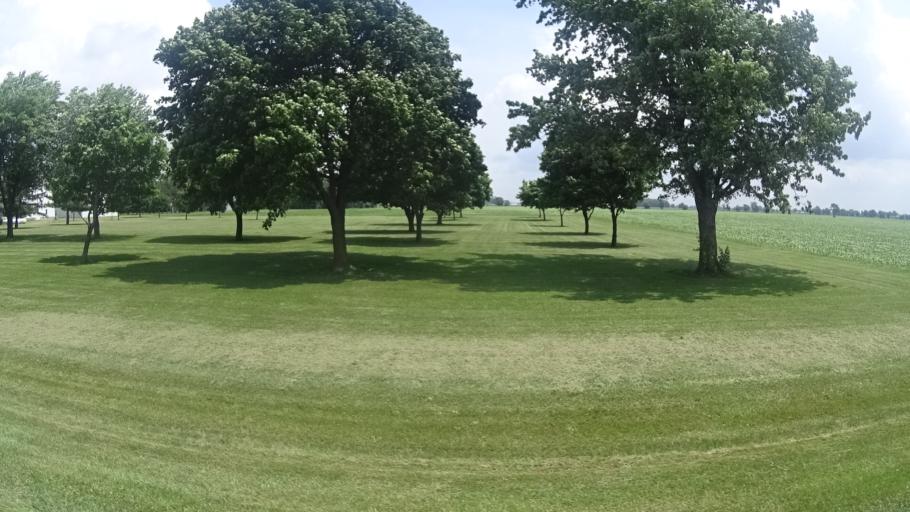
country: US
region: Ohio
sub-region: Huron County
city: Monroeville
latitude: 41.3333
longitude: -82.7474
